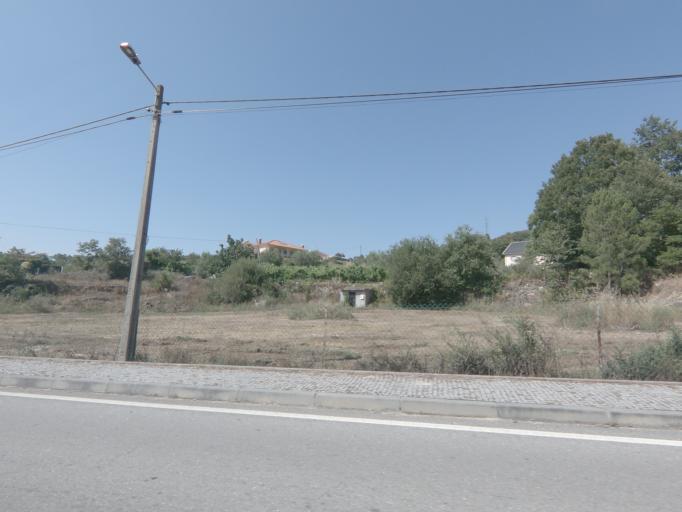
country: PT
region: Viseu
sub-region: Tarouca
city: Tarouca
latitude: 41.0218
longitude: -7.7451
